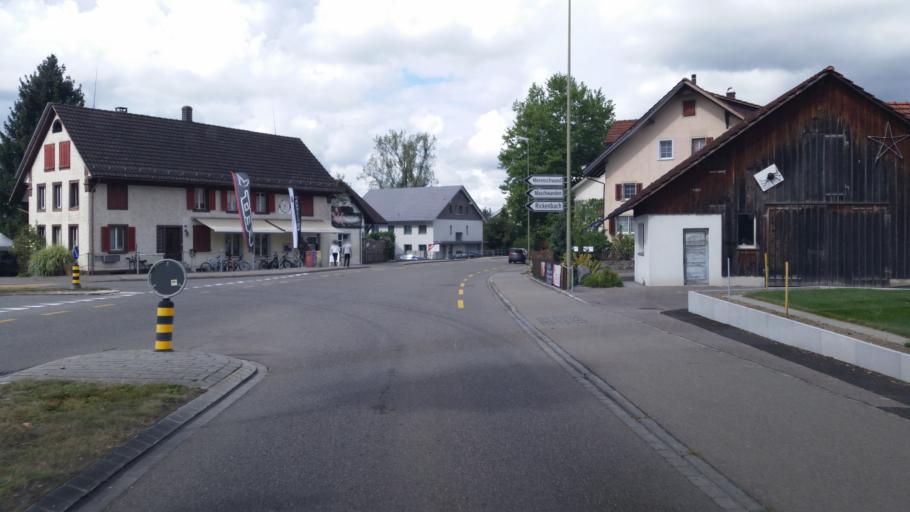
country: CH
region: Zurich
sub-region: Bezirk Affoltern
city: Ottenbach
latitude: 47.2787
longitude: 8.4057
